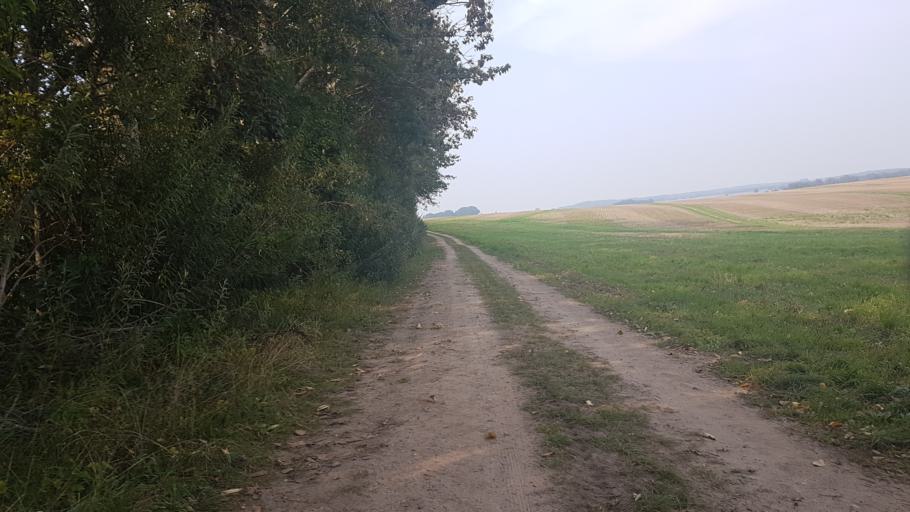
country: DE
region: Mecklenburg-Vorpommern
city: Garz
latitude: 54.2970
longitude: 13.3639
